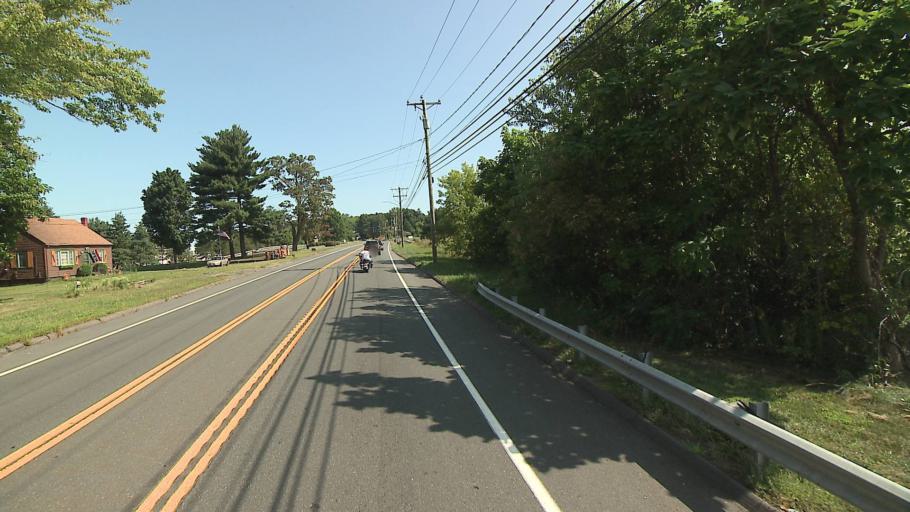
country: US
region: Connecticut
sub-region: Hartford County
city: Windsor Locks
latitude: 41.9203
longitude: -72.6084
